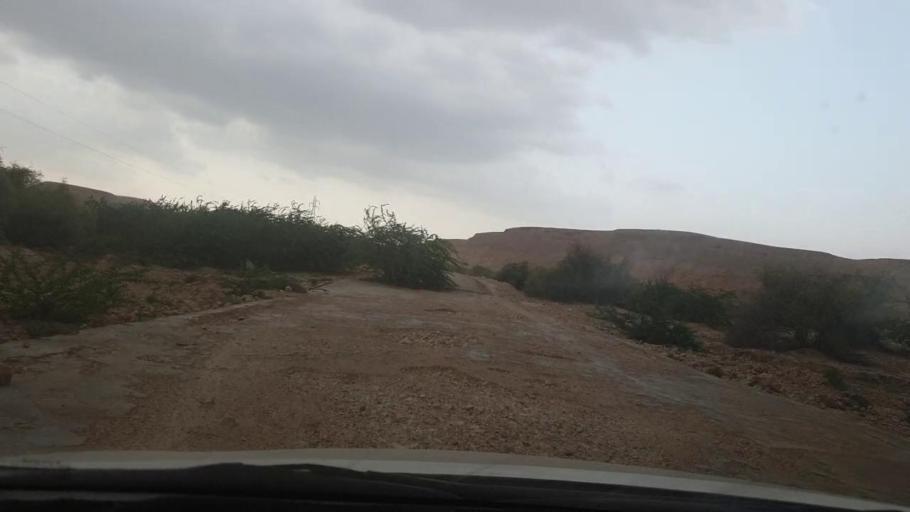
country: PK
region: Sindh
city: Khairpur
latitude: 27.4631
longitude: 68.9265
